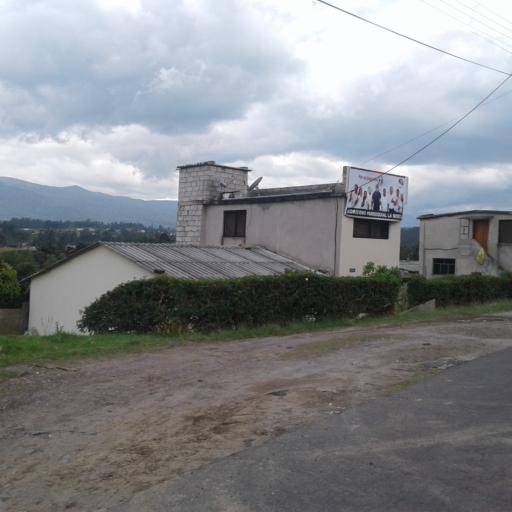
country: EC
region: Pichincha
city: Sangolqui
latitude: -0.2921
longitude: -78.3895
